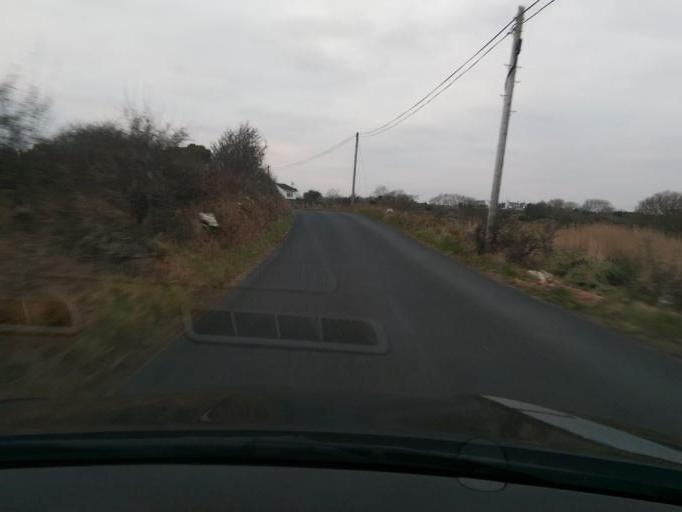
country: IE
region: Connaught
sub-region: County Galway
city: Bearna
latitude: 53.2634
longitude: -9.1528
